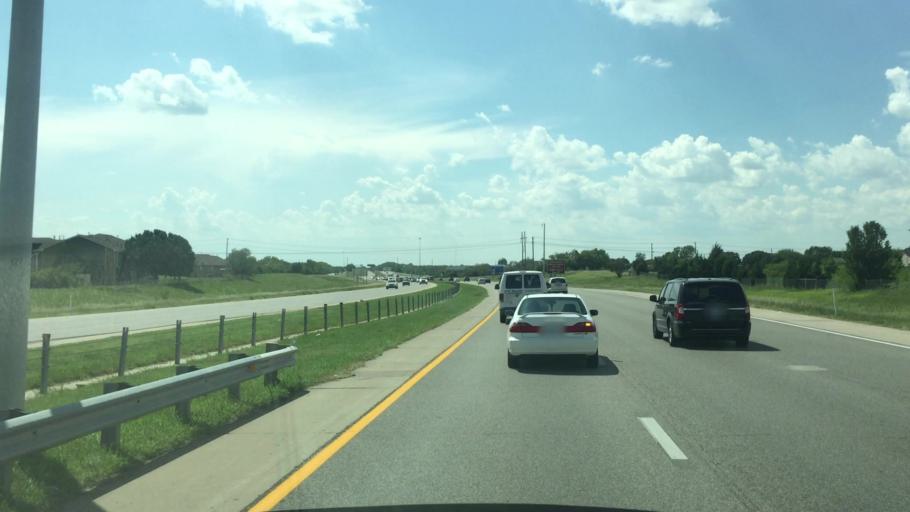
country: US
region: Kansas
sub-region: Sedgwick County
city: Bellaire
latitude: 37.7451
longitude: -97.2500
